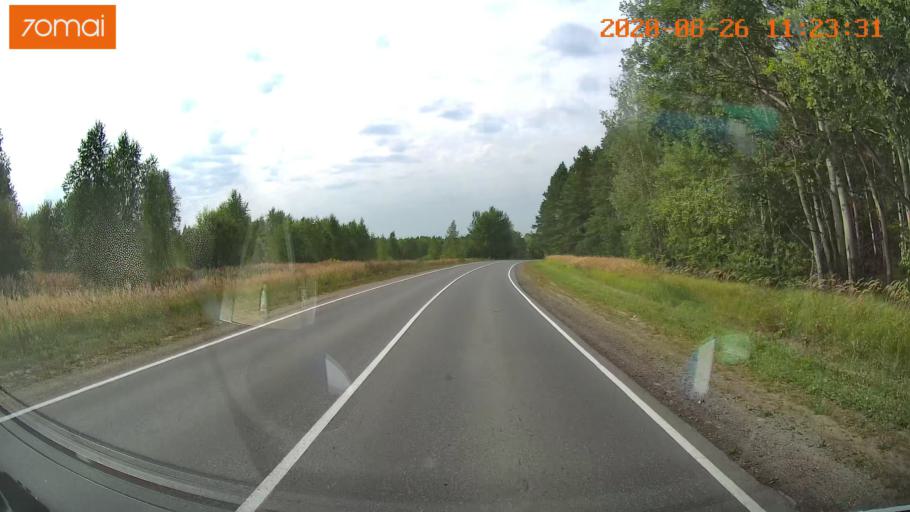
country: RU
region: Rjazan
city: Shilovo
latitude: 54.3514
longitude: 41.0092
